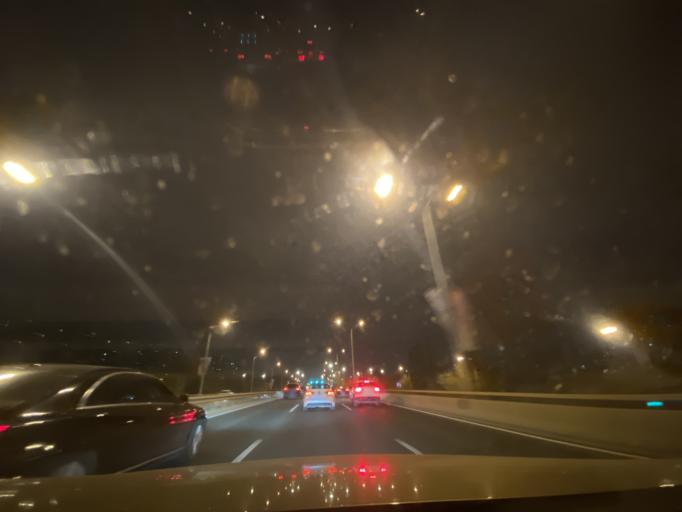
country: CN
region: Beijing
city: Lugouqiao
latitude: 39.8958
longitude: 116.2775
